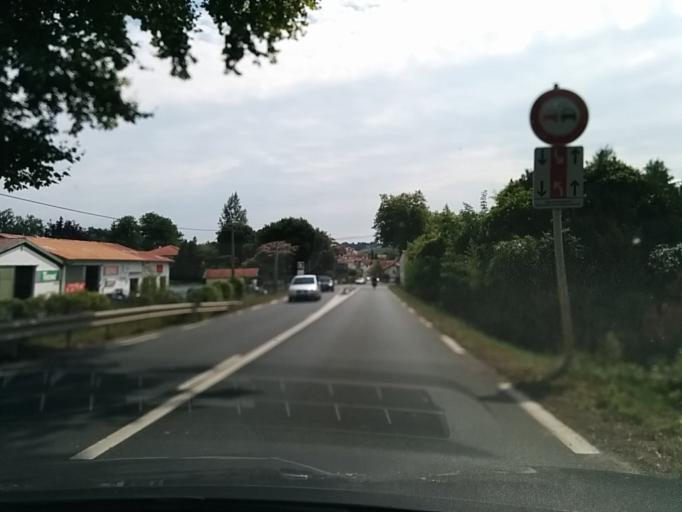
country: FR
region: Aquitaine
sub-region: Departement des Pyrenees-Atlantiques
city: Urrugne
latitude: 43.3620
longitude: -1.7071
